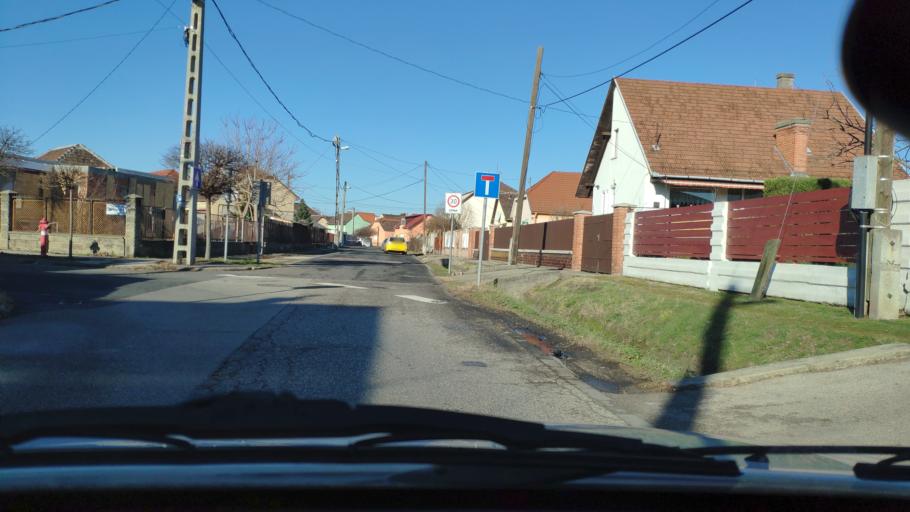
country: HU
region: Budapest
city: Budapest XXIII. keruelet
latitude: 47.4081
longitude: 19.1213
